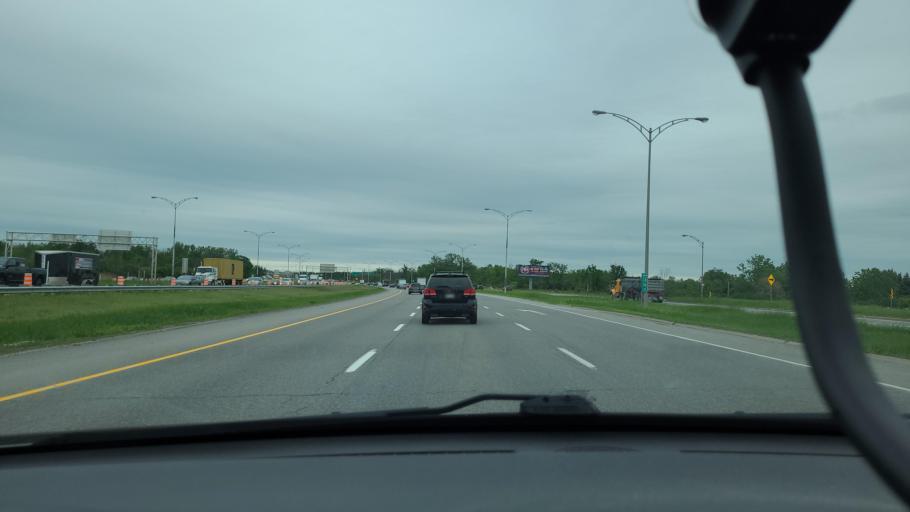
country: CA
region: Quebec
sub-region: Laval
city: Laval
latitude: 45.6189
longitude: -73.6668
